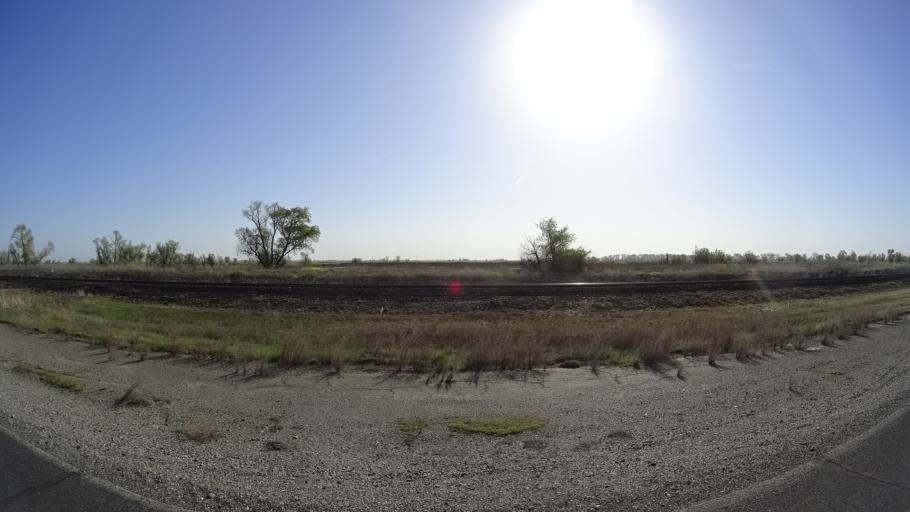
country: US
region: California
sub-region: Glenn County
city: Willows
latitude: 39.4028
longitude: -122.1927
